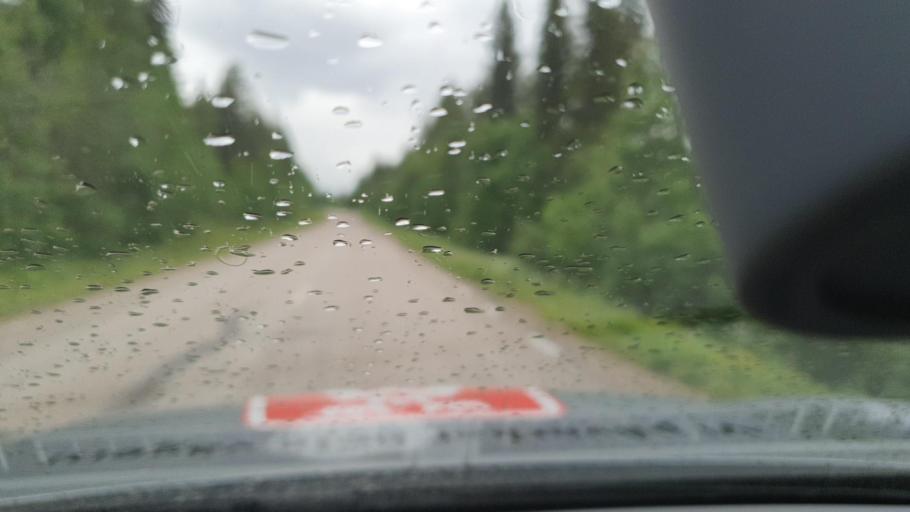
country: SE
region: Norrbotten
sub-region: Overkalix Kommun
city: OEverkalix
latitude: 66.4527
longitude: 22.7708
